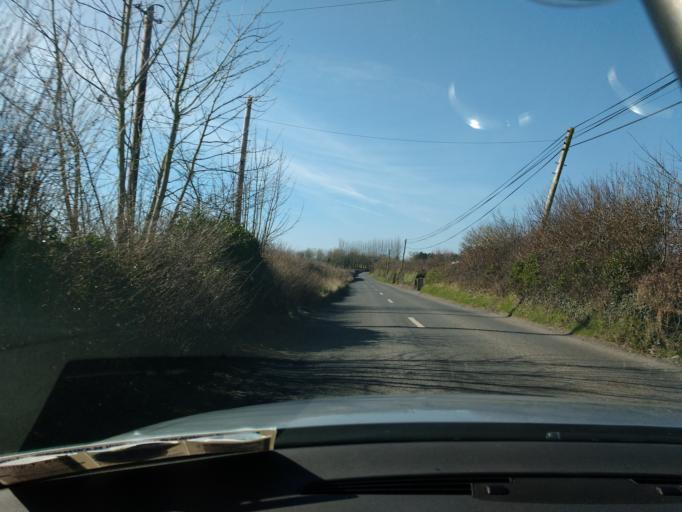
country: IE
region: Munster
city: Thurles
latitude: 52.6884
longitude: -7.8756
